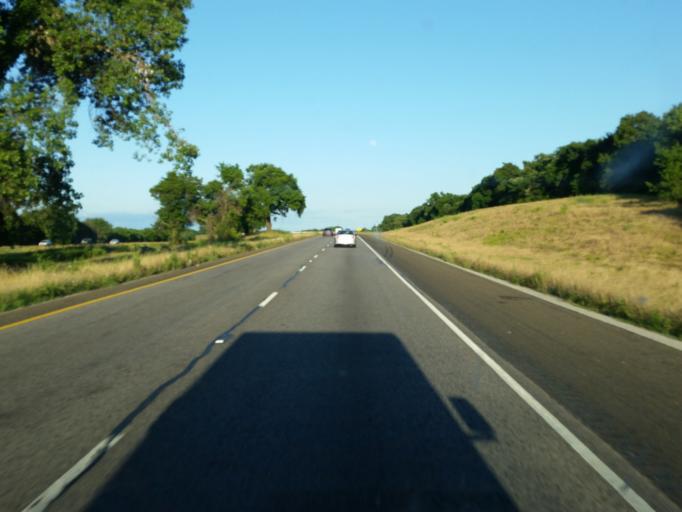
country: US
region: Texas
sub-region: Kaufman County
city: Terrell
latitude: 32.6792
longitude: -96.1892
